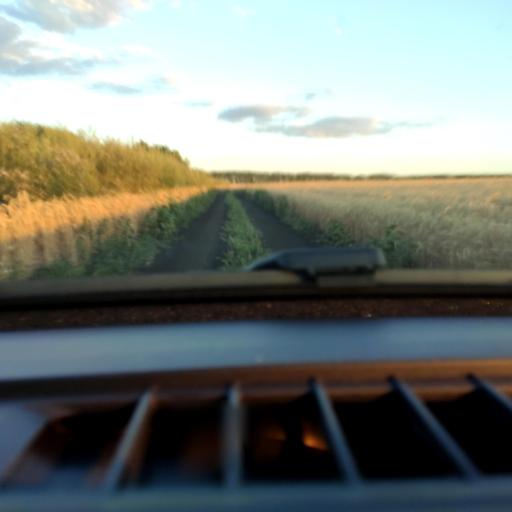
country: RU
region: Voronezj
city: Verkhnyaya Khava
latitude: 51.5854
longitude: 39.8710
